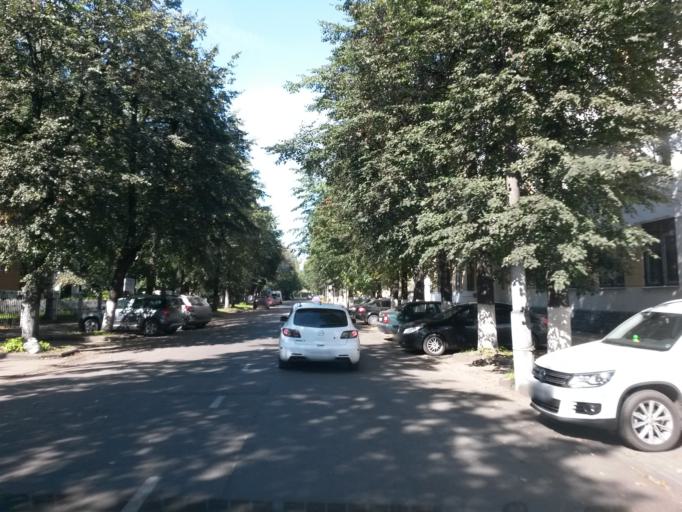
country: RU
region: Jaroslavl
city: Yaroslavl
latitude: 57.6361
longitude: 39.8879
